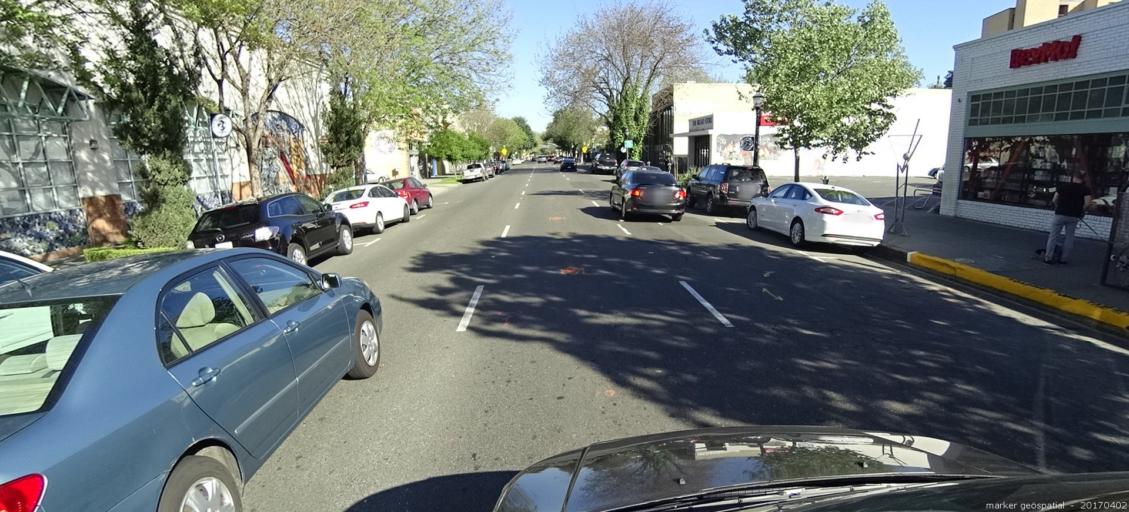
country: US
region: California
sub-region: Sacramento County
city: Sacramento
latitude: 38.5777
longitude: -121.4838
